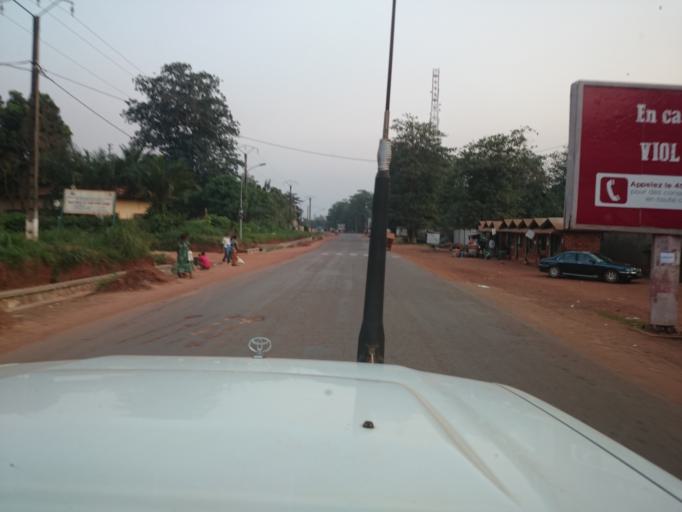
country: CF
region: Bangui
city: Bangui
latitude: 4.3758
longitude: 18.5708
